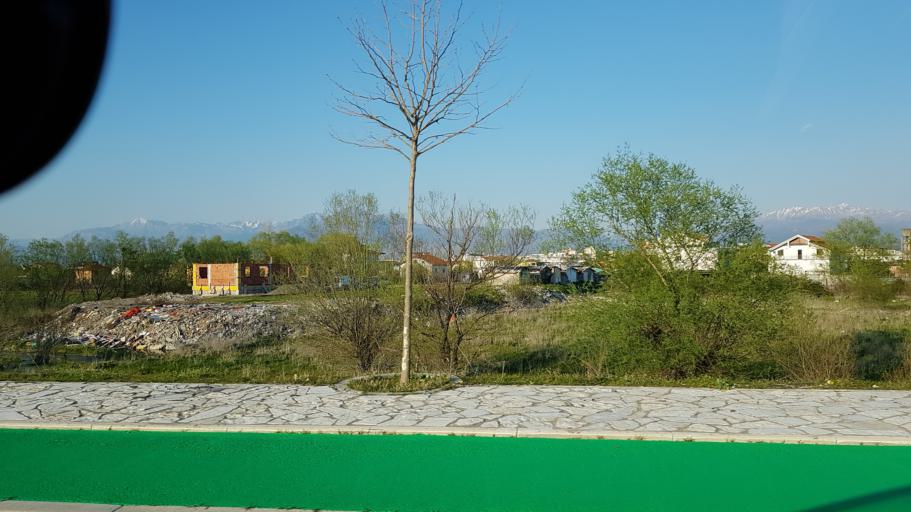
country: AL
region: Shkoder
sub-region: Rrethi i Shkodres
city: Shkoder
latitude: 42.0609
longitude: 19.4958
